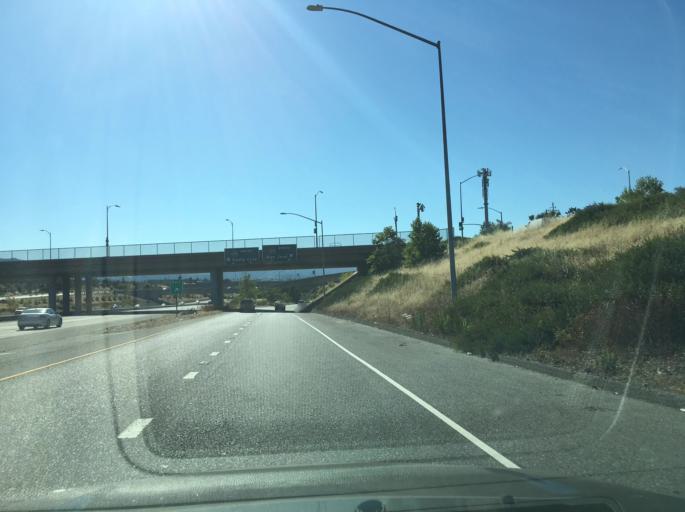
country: US
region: California
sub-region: Santa Clara County
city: Cambrian Park
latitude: 37.2546
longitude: -121.9498
